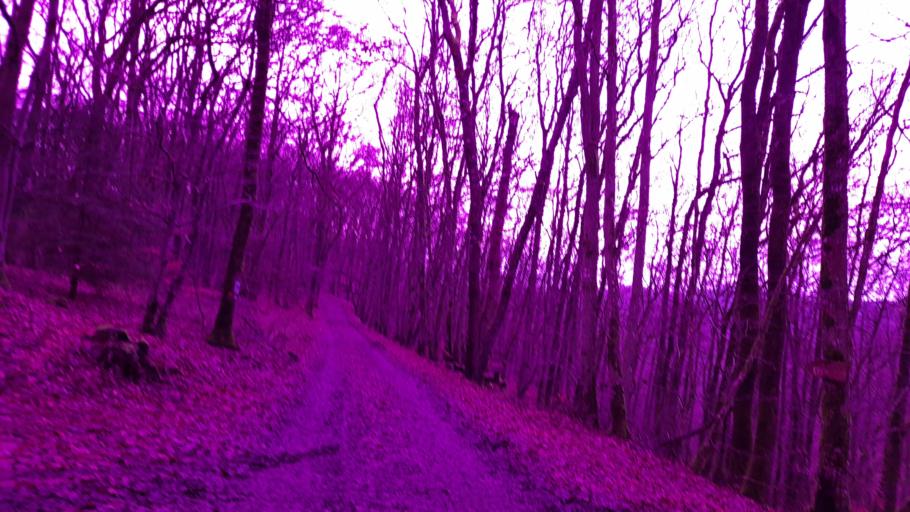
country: DE
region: Rheinland-Pfalz
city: Dasburg
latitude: 50.0684
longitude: 6.1055
